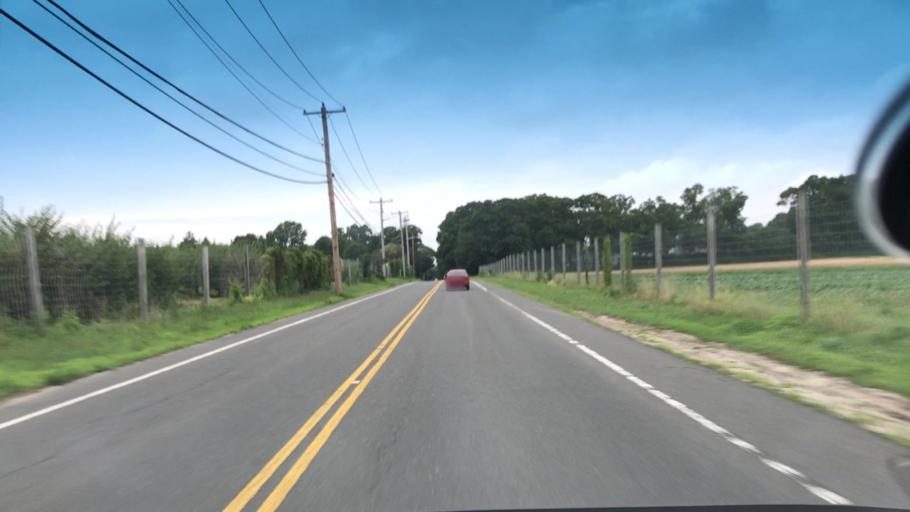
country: US
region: New York
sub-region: Suffolk County
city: Wading River
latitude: 40.9529
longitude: -72.8049
